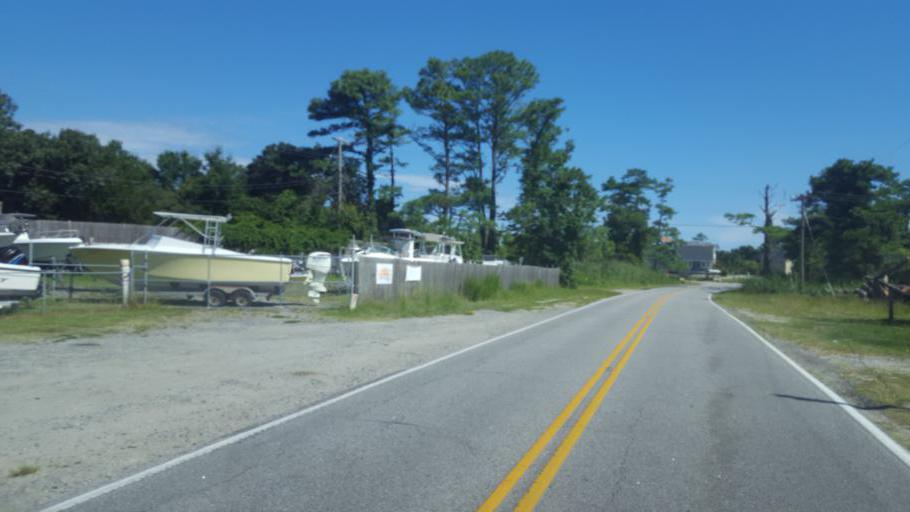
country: US
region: North Carolina
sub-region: Dare County
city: Kill Devil Hills
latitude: 36.0113
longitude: -75.6985
